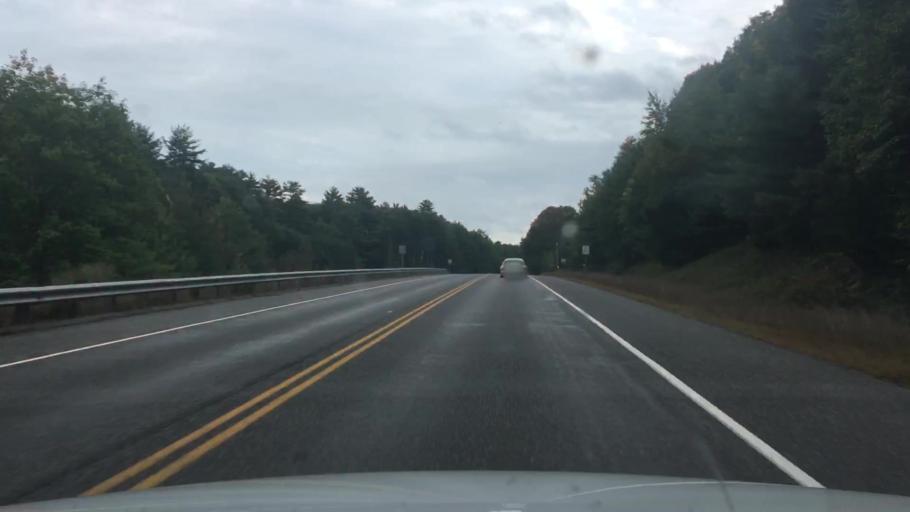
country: US
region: New Hampshire
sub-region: Carroll County
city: Wolfeboro
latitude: 43.4953
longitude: -71.2575
